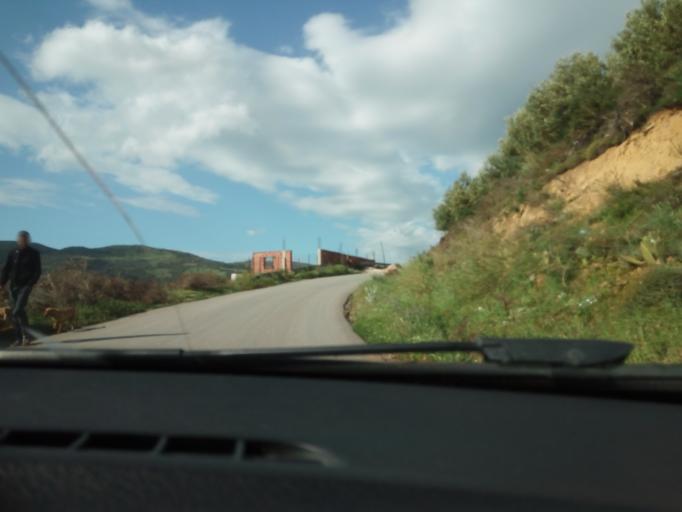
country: DZ
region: Tipaza
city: Hadjout
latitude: 36.3736
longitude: 2.4806
